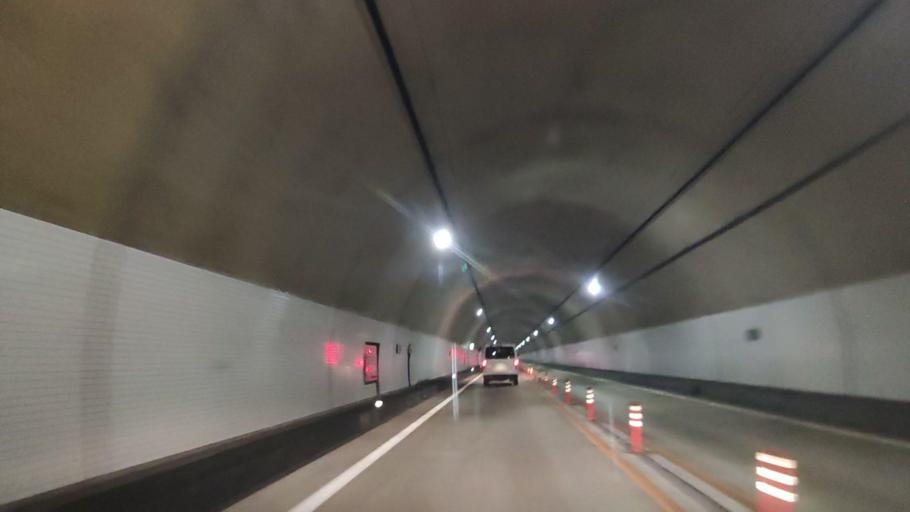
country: JP
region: Akita
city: Odate
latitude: 40.3407
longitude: 140.6334
